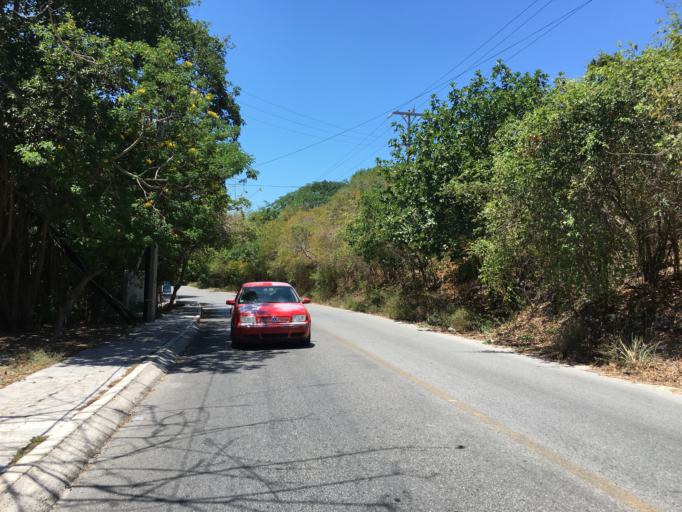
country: MX
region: Quintana Roo
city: Isla Mujeres
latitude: 21.2152
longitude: -86.7243
